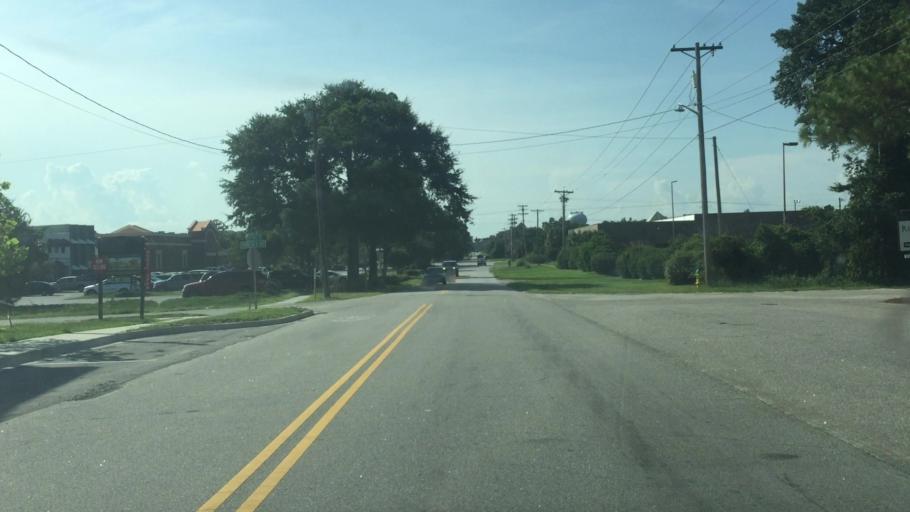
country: US
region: South Carolina
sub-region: Horry County
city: Myrtle Beach
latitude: 33.7476
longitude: -78.8144
